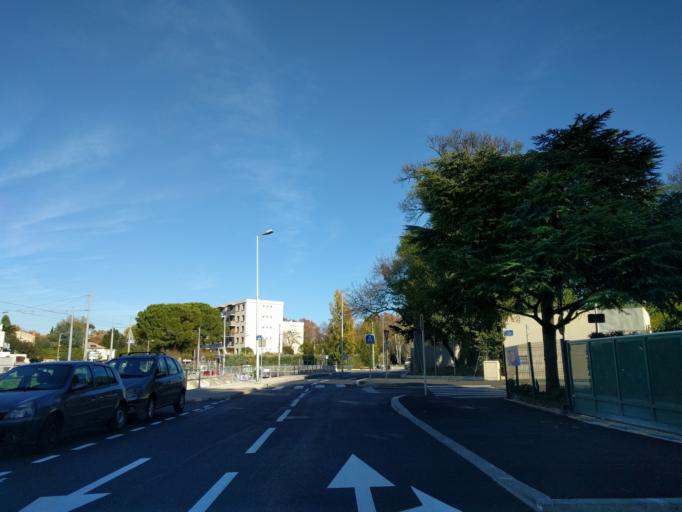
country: FR
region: Languedoc-Roussillon
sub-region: Departement de l'Herault
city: Montpellier
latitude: 43.6143
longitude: 3.8914
